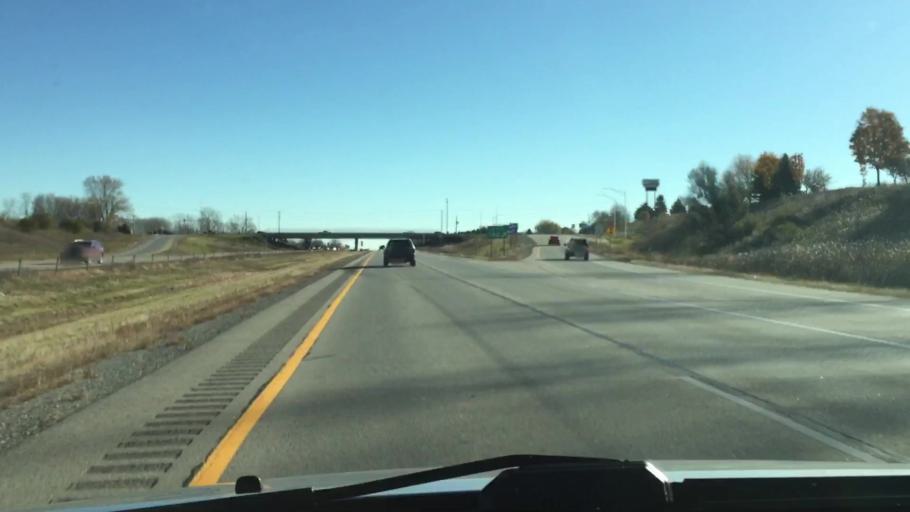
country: US
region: Wisconsin
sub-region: Outagamie County
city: Appleton
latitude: 44.2986
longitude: -88.4202
